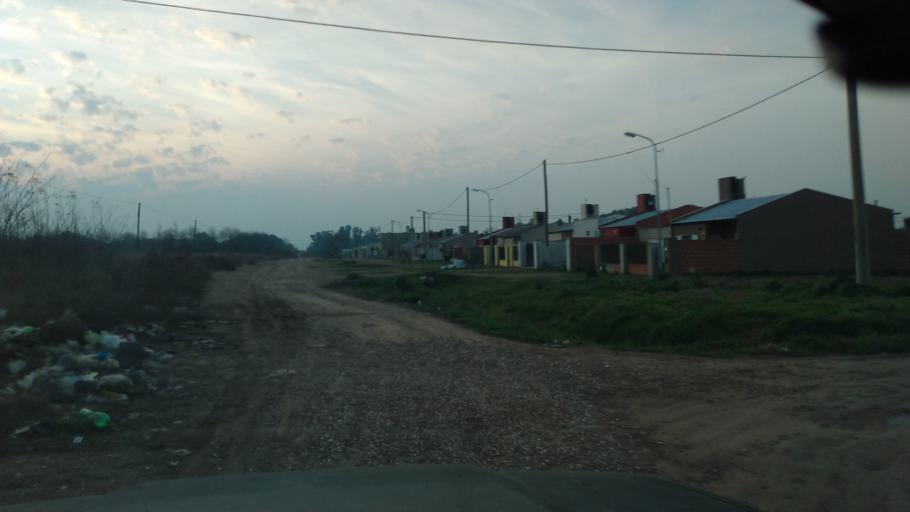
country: AR
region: Buenos Aires
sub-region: Partido de Lujan
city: Lujan
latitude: -34.5558
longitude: -59.1370
